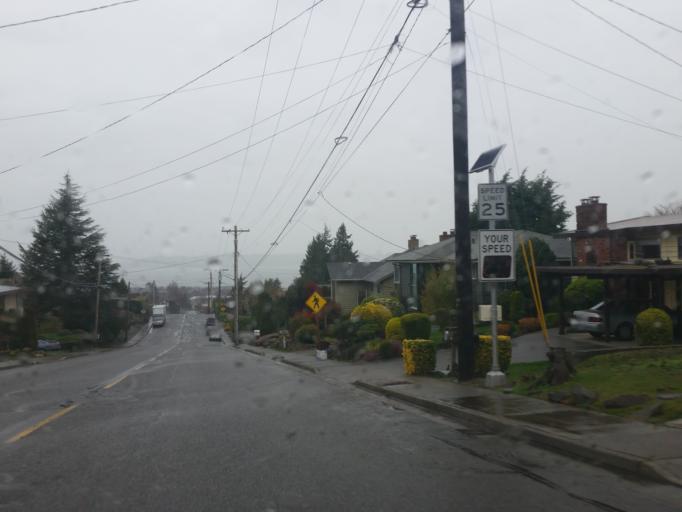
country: US
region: Washington
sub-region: Snohomish County
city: Edmonds
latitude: 47.8074
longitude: -122.3683
